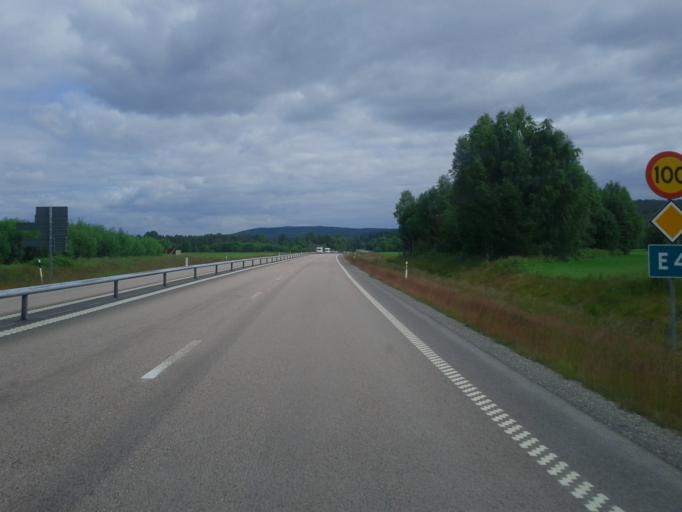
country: SE
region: Vaesternorrland
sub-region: OErnskoeldsviks Kommun
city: Bjasta
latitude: 63.2085
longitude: 18.4891
